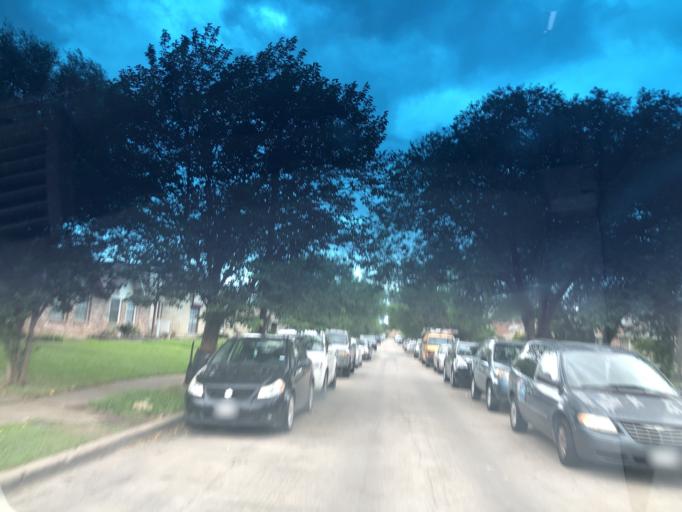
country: US
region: Texas
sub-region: Dallas County
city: Grand Prairie
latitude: 32.6991
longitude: -97.0086
